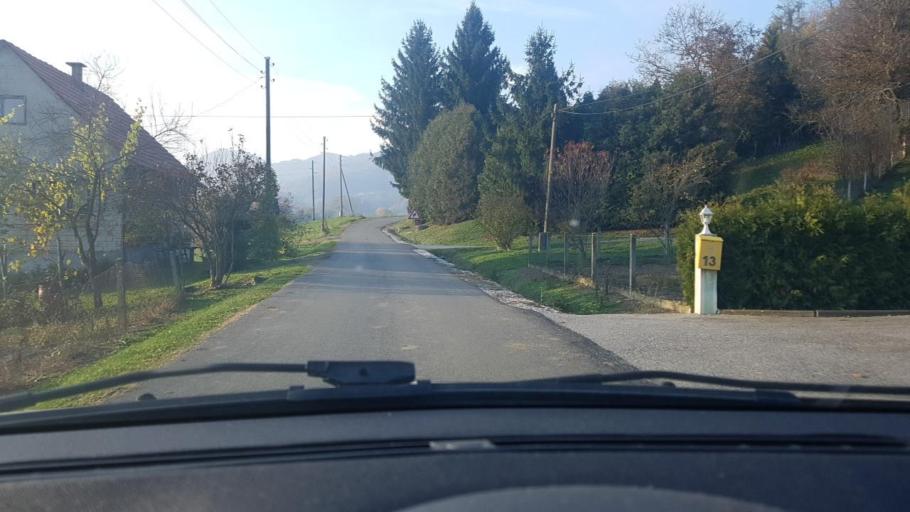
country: SI
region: Podcetrtek
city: Podcetrtek
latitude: 46.1442
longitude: 15.6004
